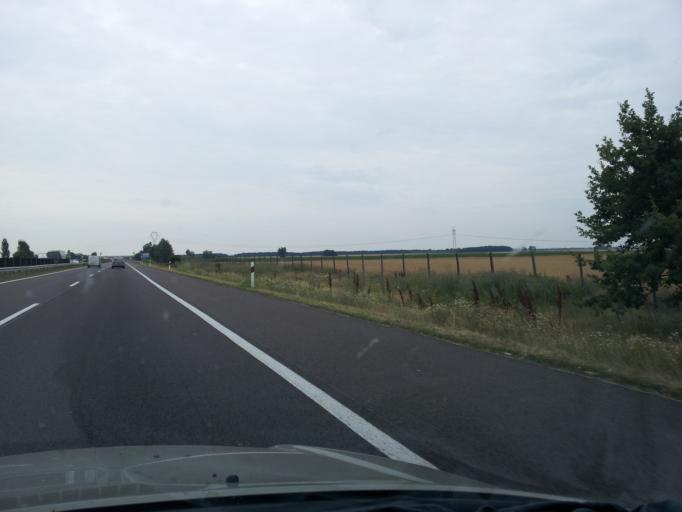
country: HU
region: Heves
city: Adacs
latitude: 47.7213
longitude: 19.9905
